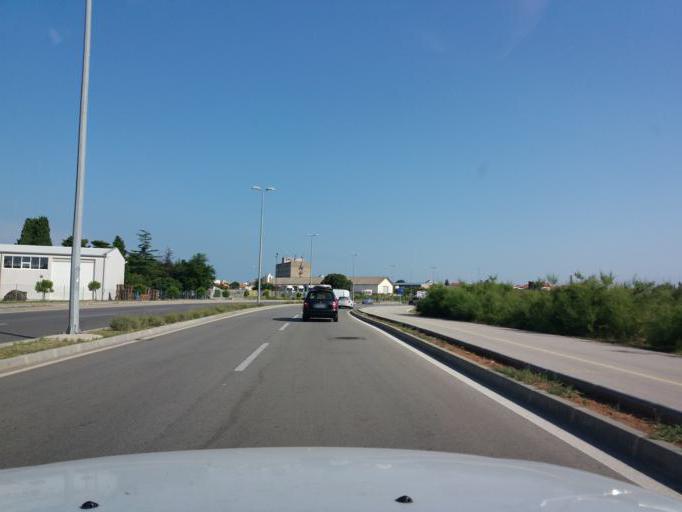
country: HR
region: Zadarska
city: Zadar
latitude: 44.0978
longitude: 15.2567
